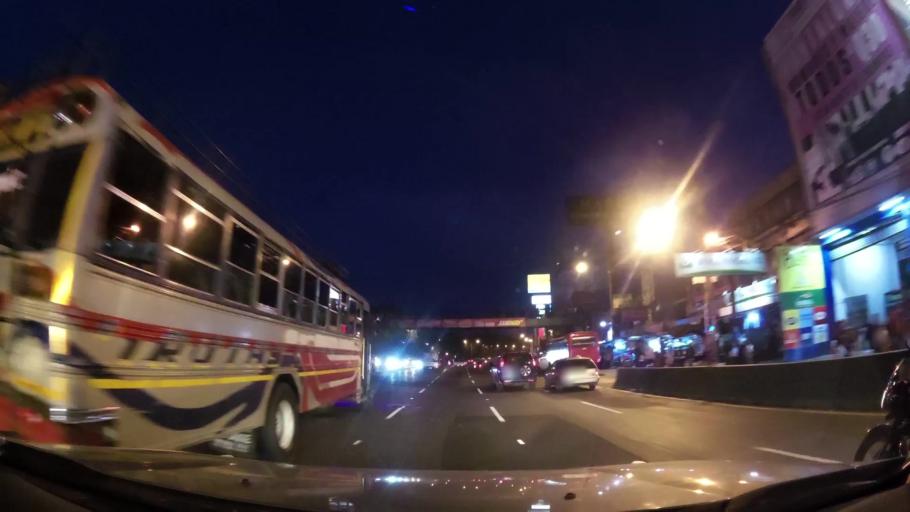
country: GT
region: Guatemala
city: Guatemala City
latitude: 14.6158
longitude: -90.5387
